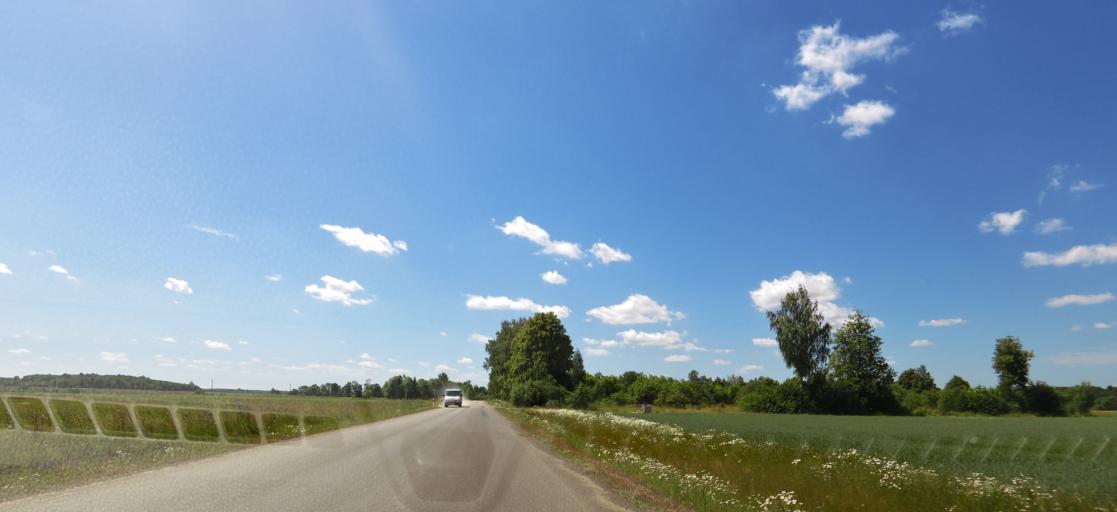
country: LT
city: Kupiskis
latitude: 55.9576
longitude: 24.9881
